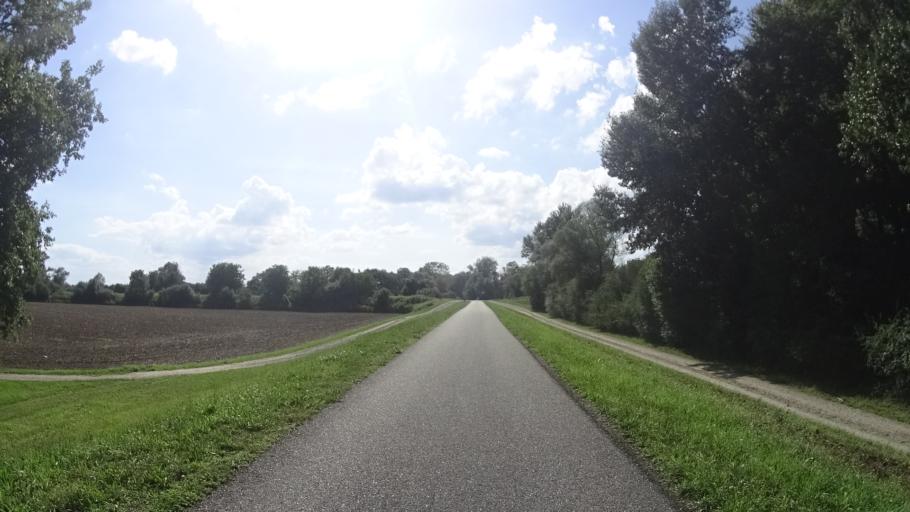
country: FR
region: Alsace
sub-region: Departement du Bas-Rhin
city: Seltz
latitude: 48.8685
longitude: 8.1057
